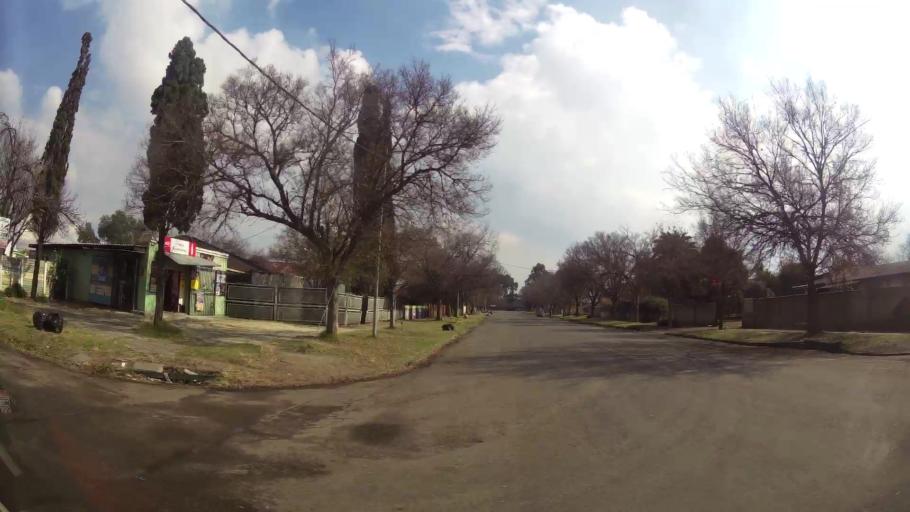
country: ZA
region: Gauteng
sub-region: Sedibeng District Municipality
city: Vereeniging
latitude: -26.6758
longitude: 27.9203
